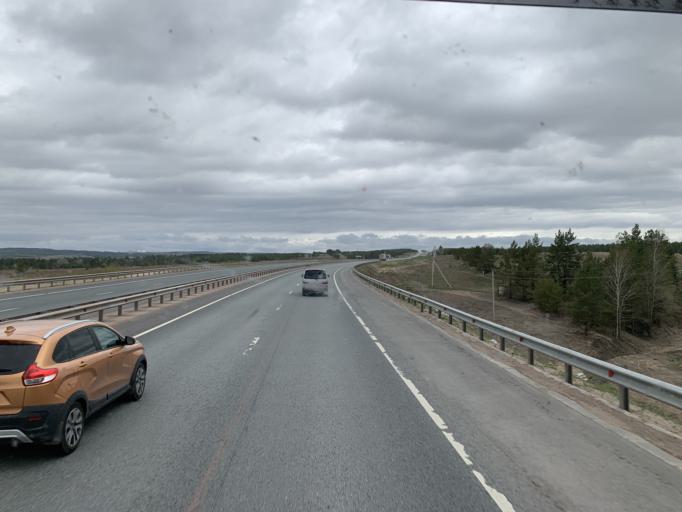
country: RU
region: Ulyanovsk
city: Novospasskoye
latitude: 53.1505
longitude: 47.6618
